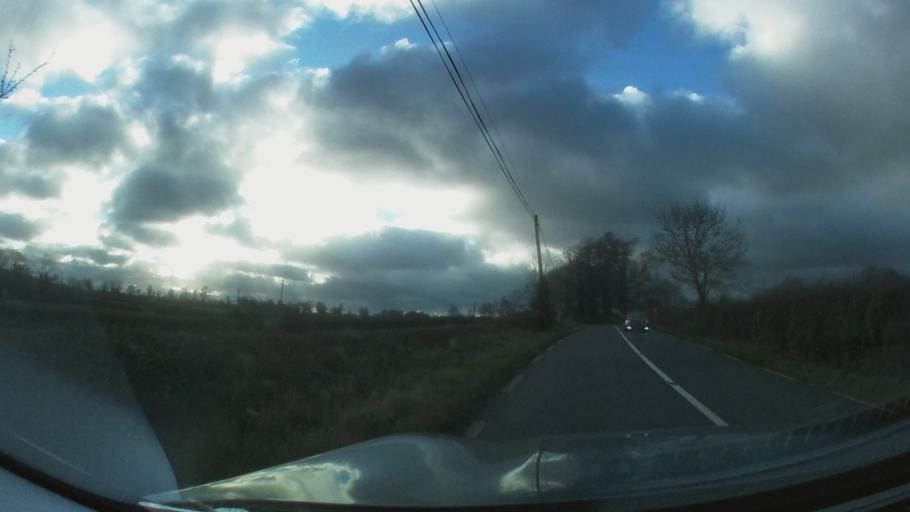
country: IE
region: Leinster
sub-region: Kilkenny
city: Thomastown
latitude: 52.6112
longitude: -7.0792
